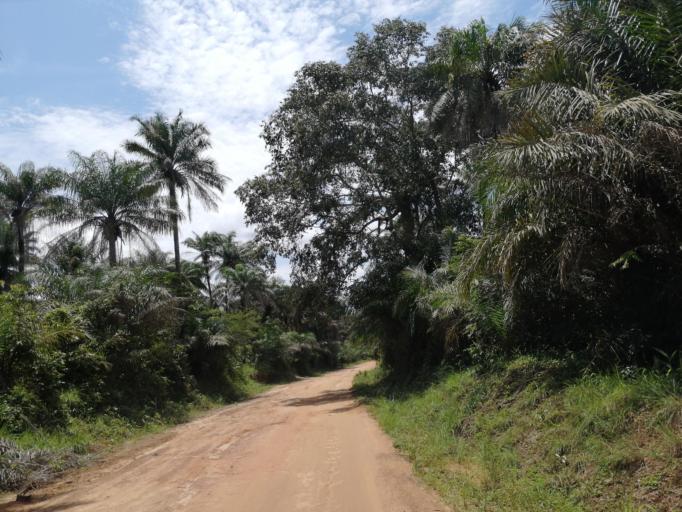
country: SL
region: Northern Province
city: Konakridee
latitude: 8.7547
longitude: -13.1433
